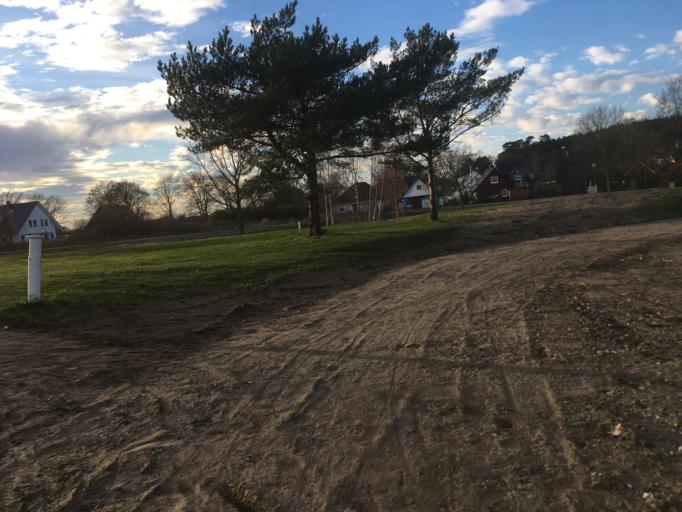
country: DE
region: Mecklenburg-Vorpommern
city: Ostseebad Sellin
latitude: 54.3736
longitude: 13.6932
